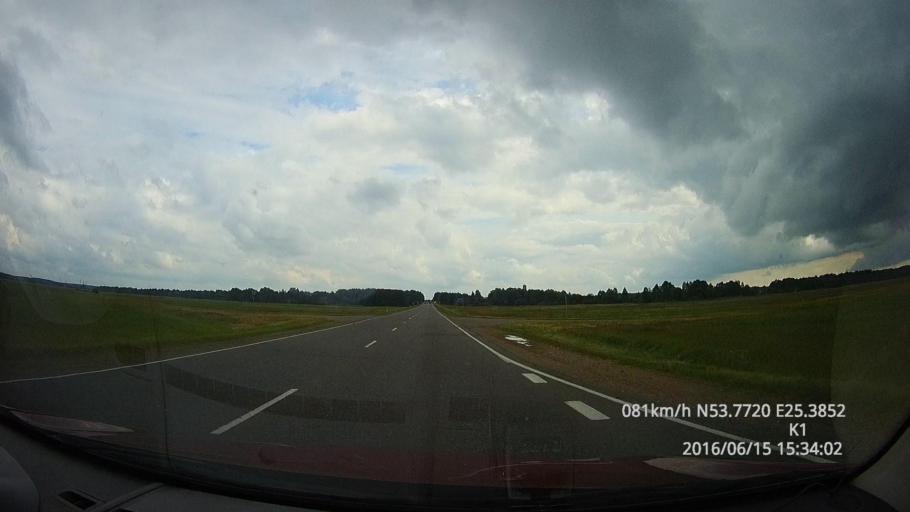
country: BY
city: Berezovka
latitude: 53.7714
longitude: 25.3855
